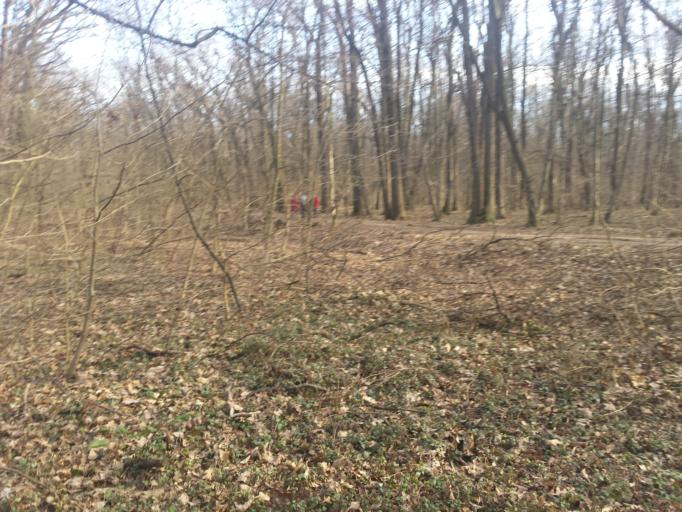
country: RO
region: Ilfov
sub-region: Comuna Otopeni
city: Otopeni
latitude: 44.5220
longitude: 26.0917
